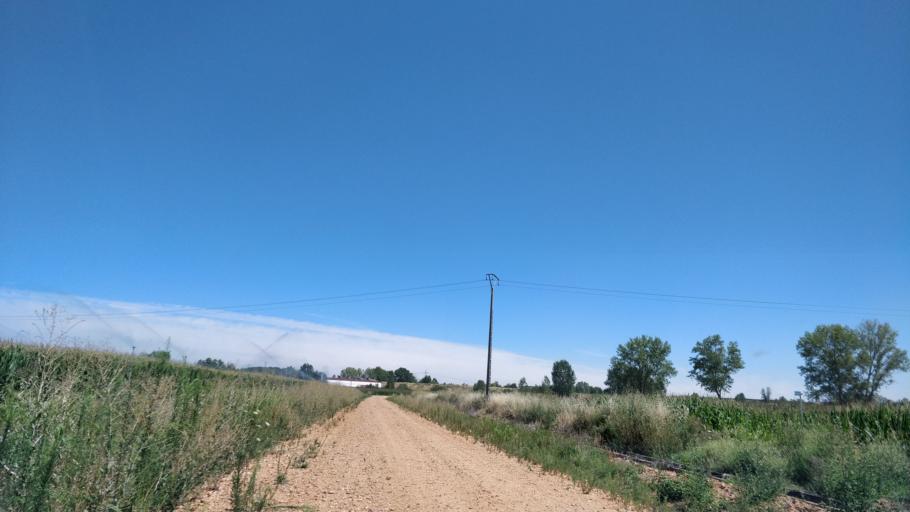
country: ES
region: Castille and Leon
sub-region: Provincia de Leon
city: Bustillo del Paramo
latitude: 42.4742
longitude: -5.8117
